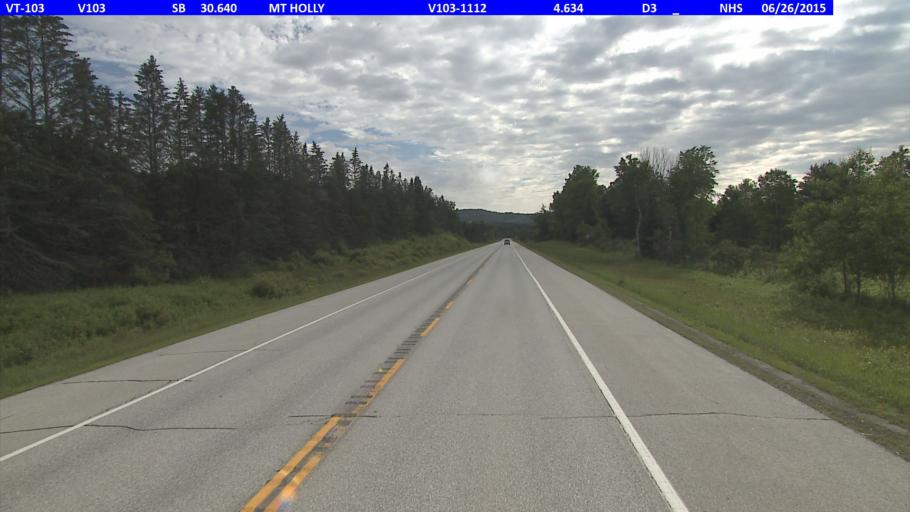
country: US
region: Vermont
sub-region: Rutland County
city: Rutland
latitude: 43.4502
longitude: -72.8141
